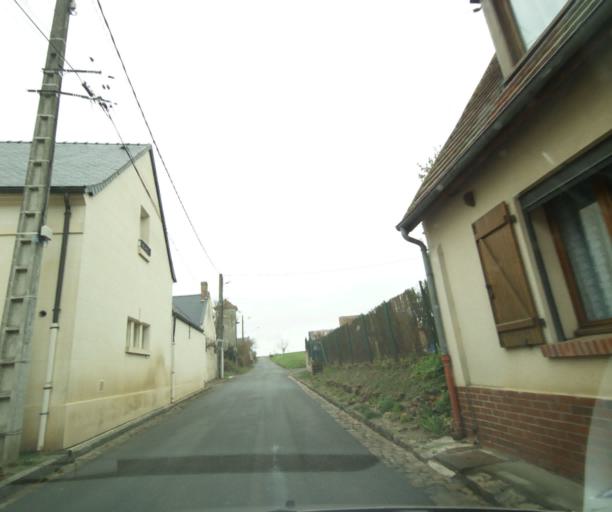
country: FR
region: Picardie
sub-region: Departement de l'Oise
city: Noyon
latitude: 49.5990
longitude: 3.0151
